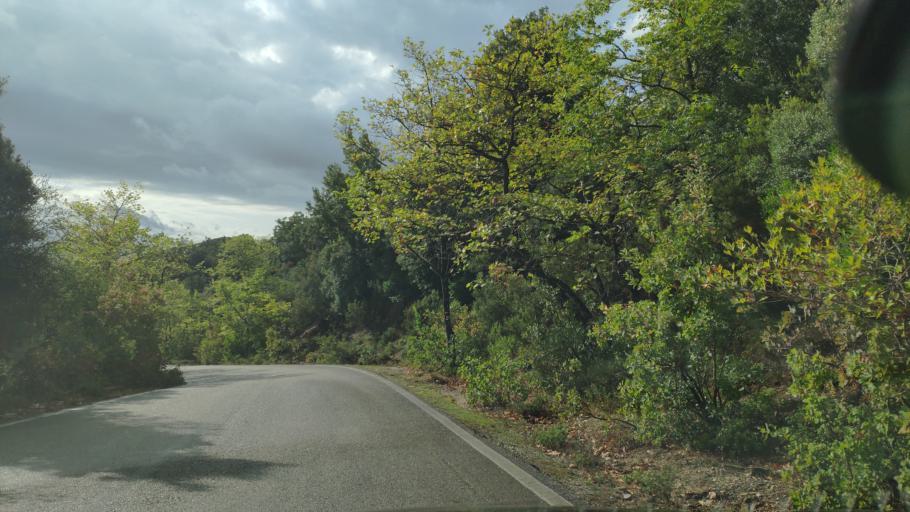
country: GR
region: West Greece
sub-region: Nomos Aitolias kai Akarnanias
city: Sardinia
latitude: 38.8602
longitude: 21.3042
